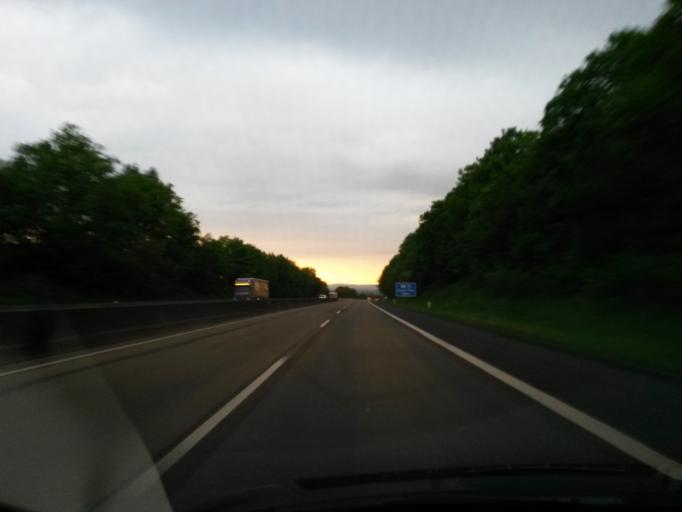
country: DE
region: Hesse
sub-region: Regierungsbezirk Kassel
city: Eichenzell
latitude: 50.4689
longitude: 9.7156
